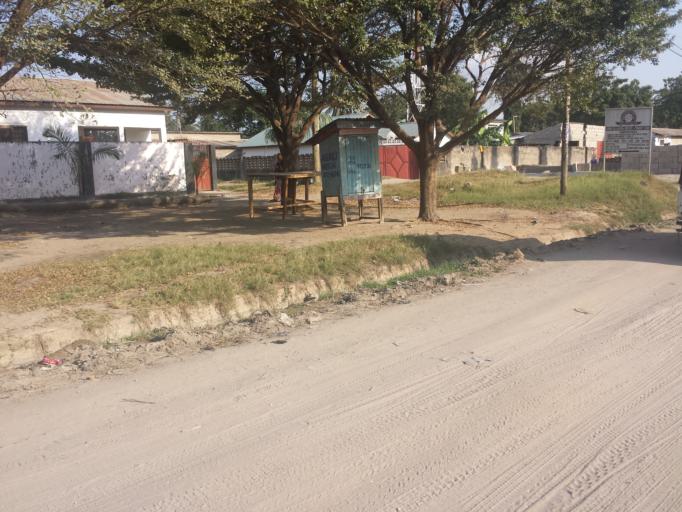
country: TZ
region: Dar es Salaam
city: Magomeni
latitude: -6.8329
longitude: 39.2213
